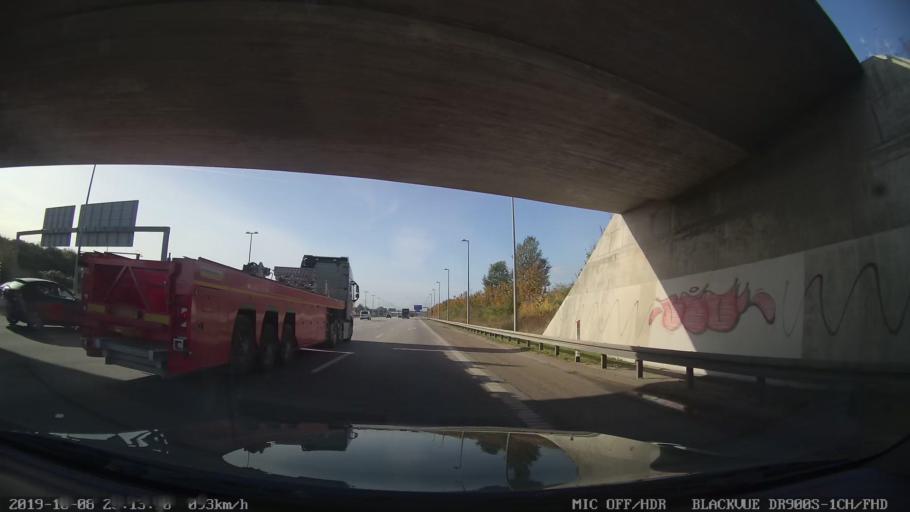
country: DK
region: Zealand
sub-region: Greve Kommune
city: Greve
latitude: 55.6092
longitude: 12.3145
